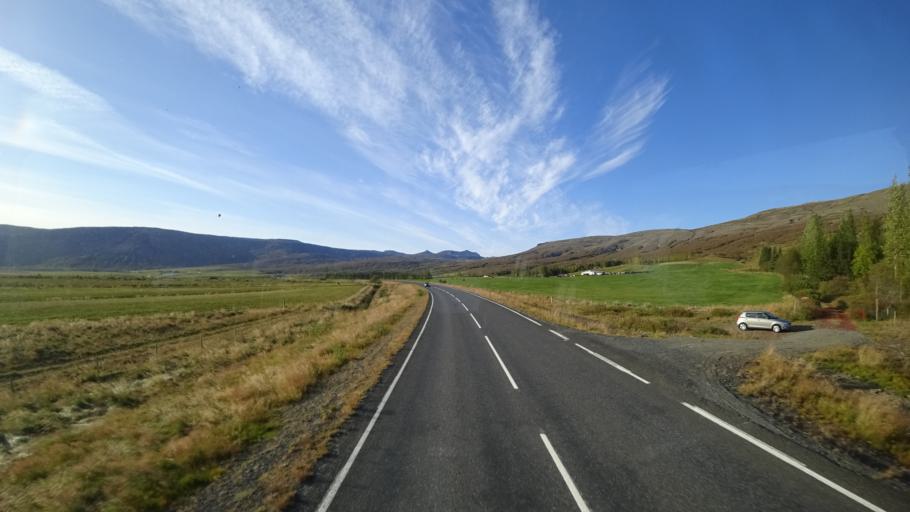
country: IS
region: South
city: Selfoss
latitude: 64.2338
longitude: -20.6373
